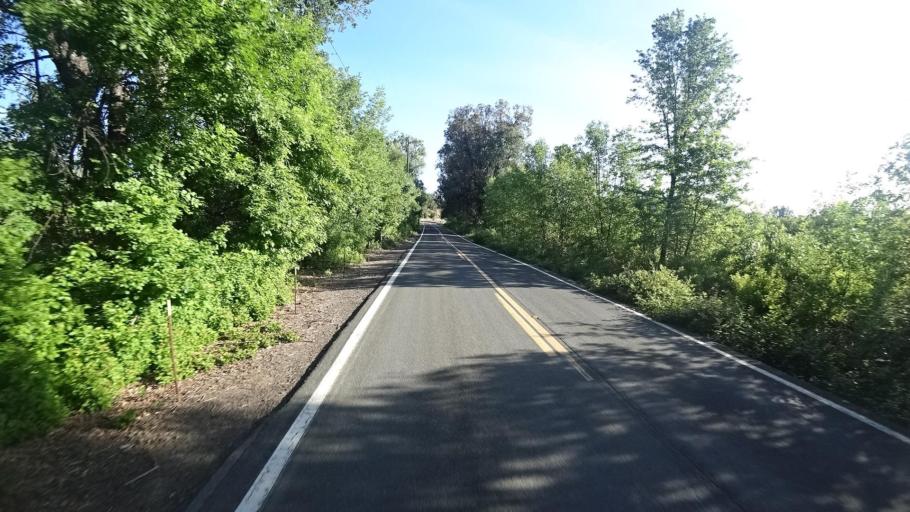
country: US
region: California
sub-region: Lake County
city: North Lakeport
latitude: 39.0870
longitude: -122.9499
